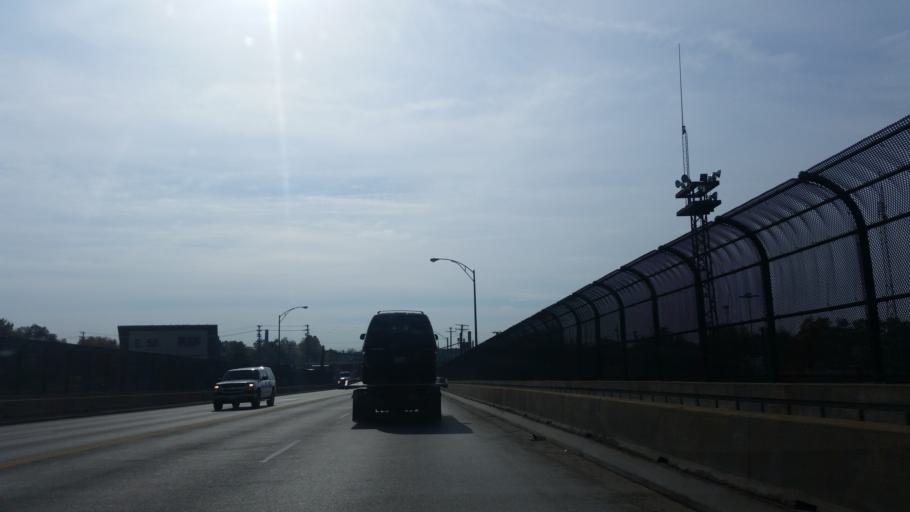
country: US
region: Ohio
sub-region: Cuyahoga County
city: Newburgh Heights
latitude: 41.4818
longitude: -81.6516
